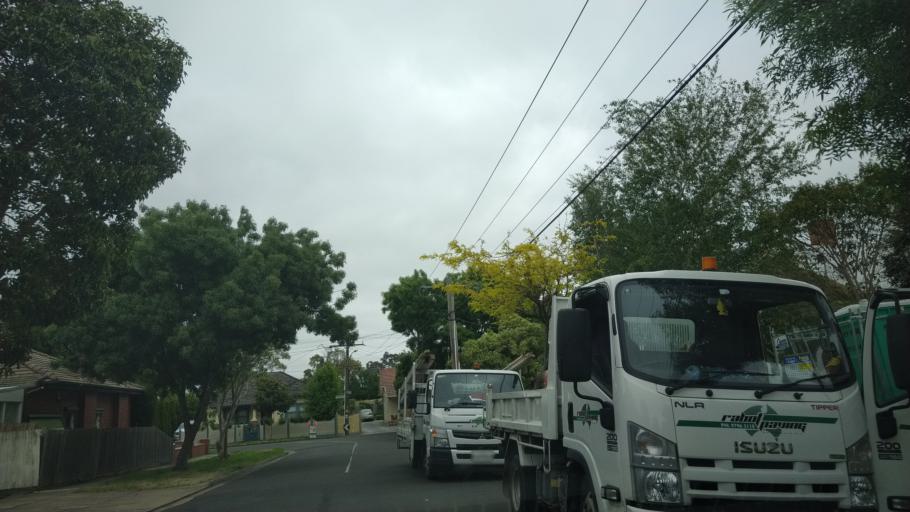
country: AU
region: Victoria
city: Hughesdale
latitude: -37.9045
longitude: 145.0809
